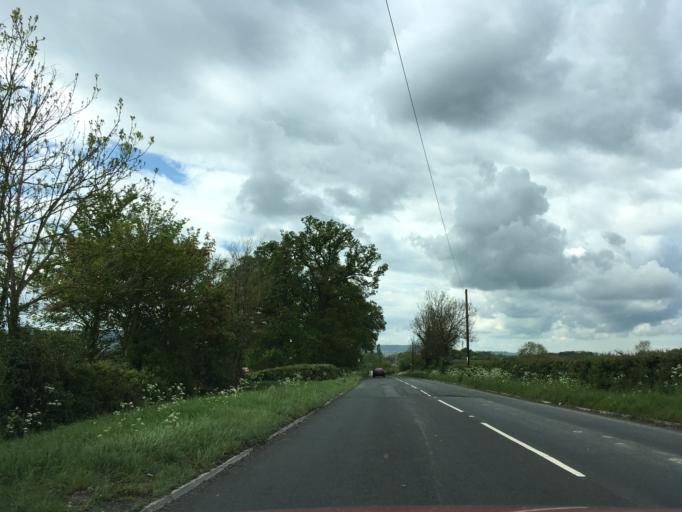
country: GB
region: England
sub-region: Gloucestershire
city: Stonehouse
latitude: 51.7621
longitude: -2.2827
